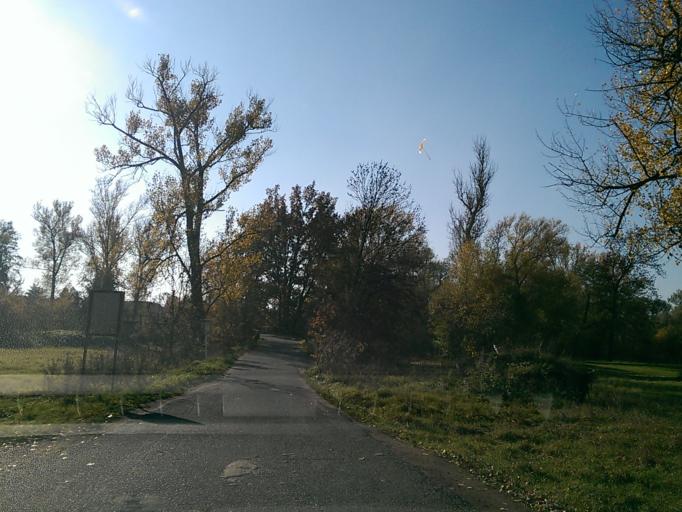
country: CZ
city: Prisovice
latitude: 50.5647
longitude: 15.0853
